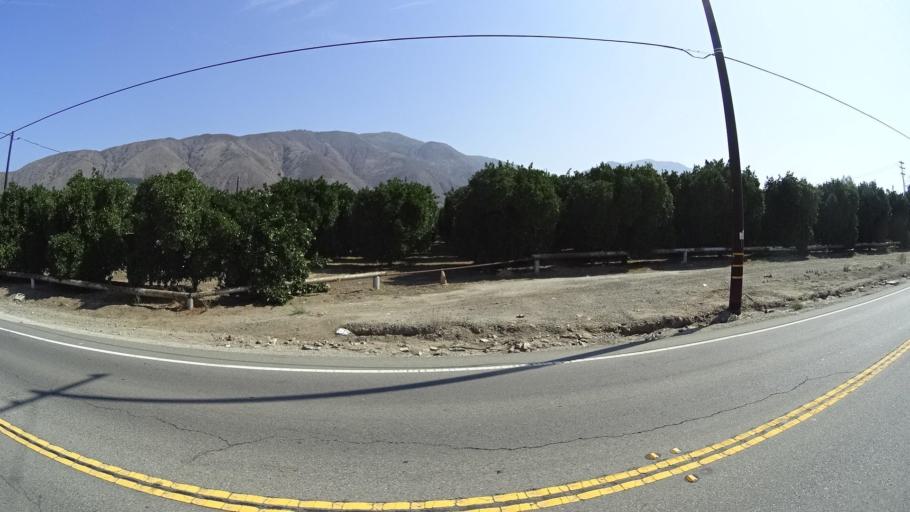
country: US
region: California
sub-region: San Diego County
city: Valley Center
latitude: 33.3297
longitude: -117.0022
